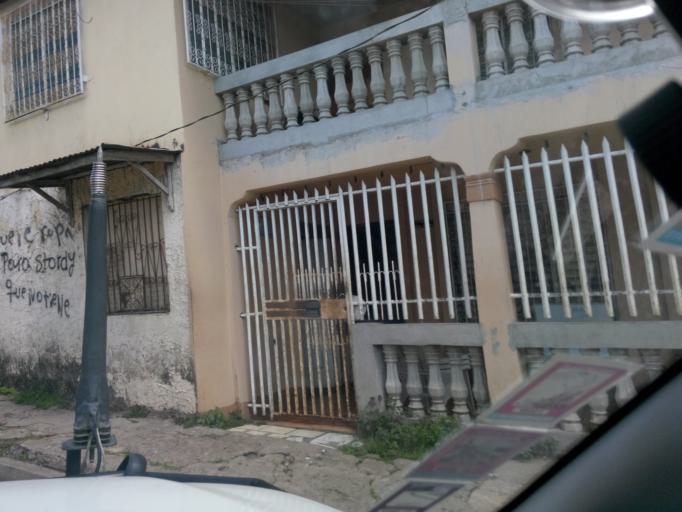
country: NI
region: Atlantico Sur
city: Bluefields
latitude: 12.0149
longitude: -83.7591
